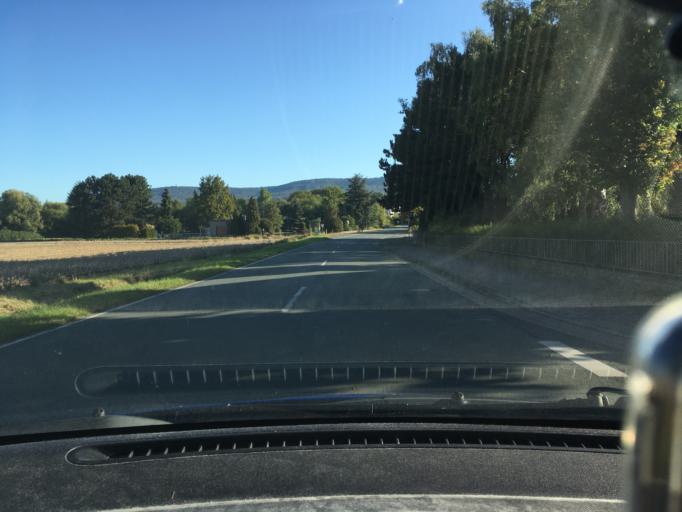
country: DE
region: Lower Saxony
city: Hulsede
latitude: 52.2560
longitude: 9.3688
